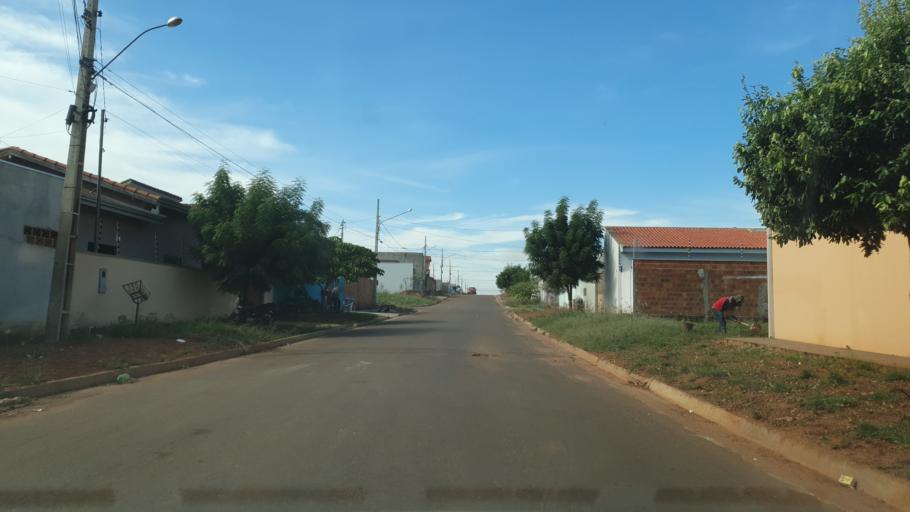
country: BR
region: Mato Grosso
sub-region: Pontes E Lacerda
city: Pontes e Lacerda
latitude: -15.2487
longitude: -59.3185
